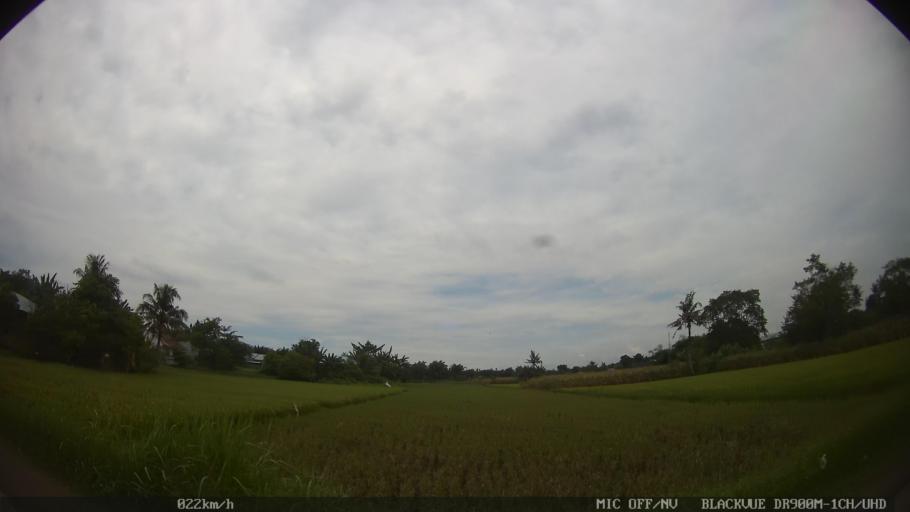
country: ID
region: North Sumatra
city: Sunggal
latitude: 3.6302
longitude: 98.5600
